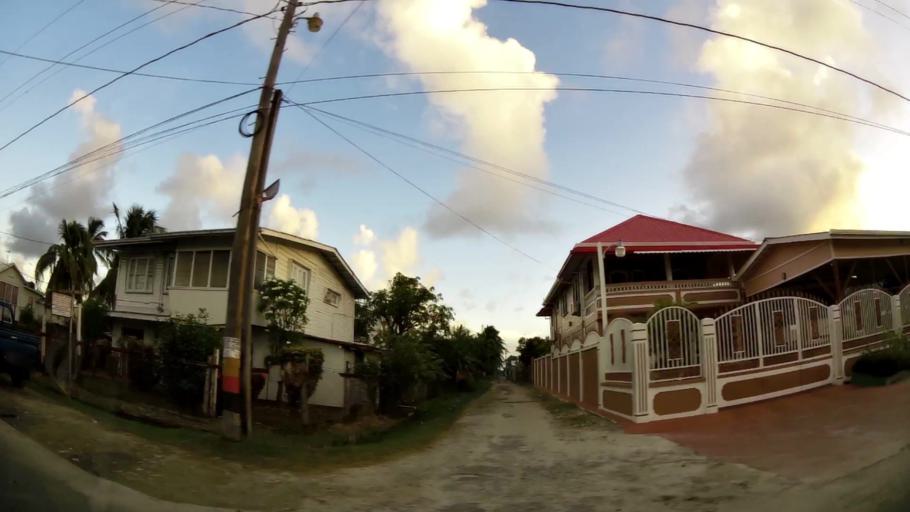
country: GY
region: Demerara-Mahaica
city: Georgetown
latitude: 6.8157
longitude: -58.1067
